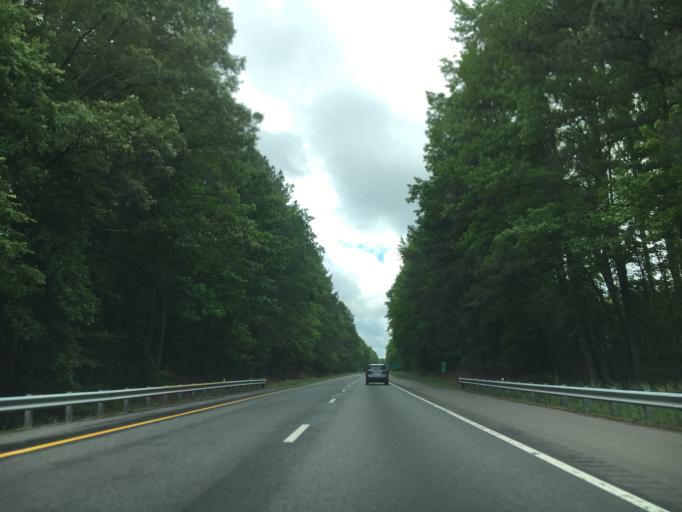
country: US
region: Virginia
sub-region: Mecklenburg County
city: South Hill
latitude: 36.7344
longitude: -78.1029
